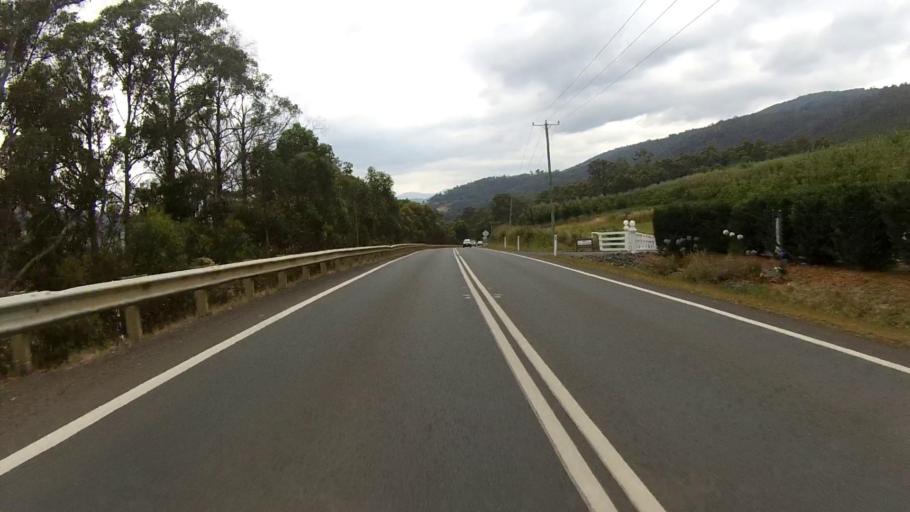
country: AU
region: Tasmania
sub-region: Huon Valley
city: Huonville
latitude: -43.0626
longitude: 147.0403
